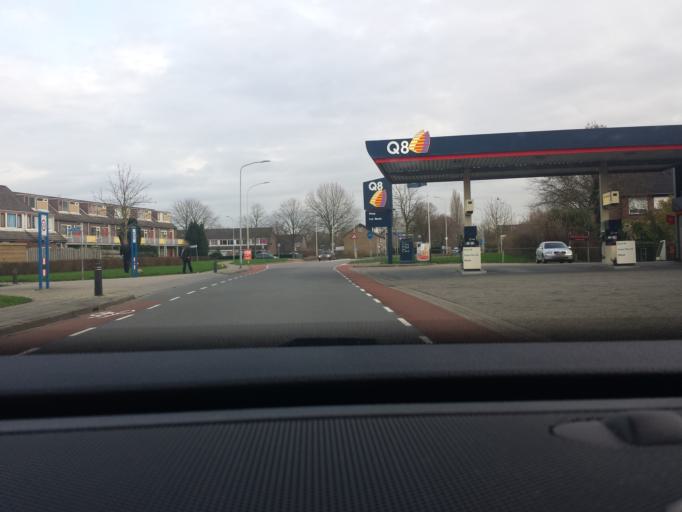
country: NL
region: Gelderland
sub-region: Gemeente Duiven
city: Duiven
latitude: 51.9467
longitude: 6.0267
